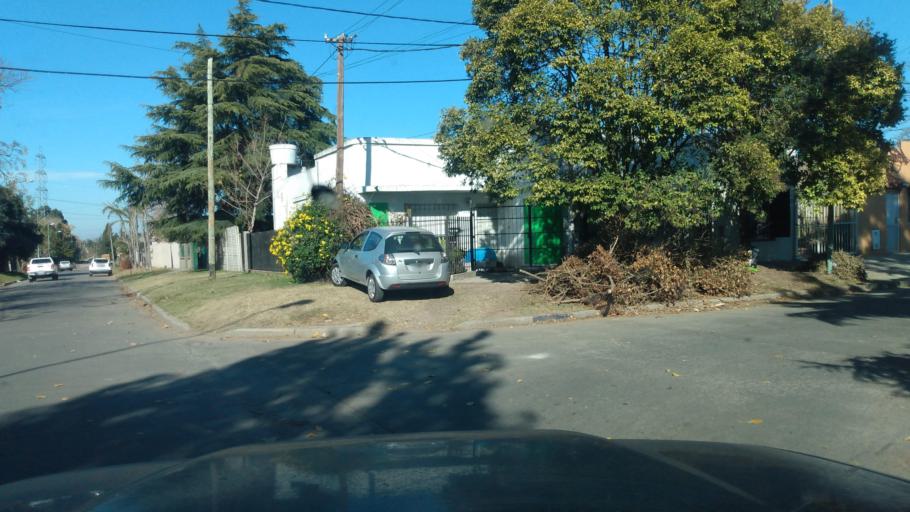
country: AR
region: Buenos Aires
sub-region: Partido de Lujan
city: Lujan
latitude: -34.5834
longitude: -59.1091
